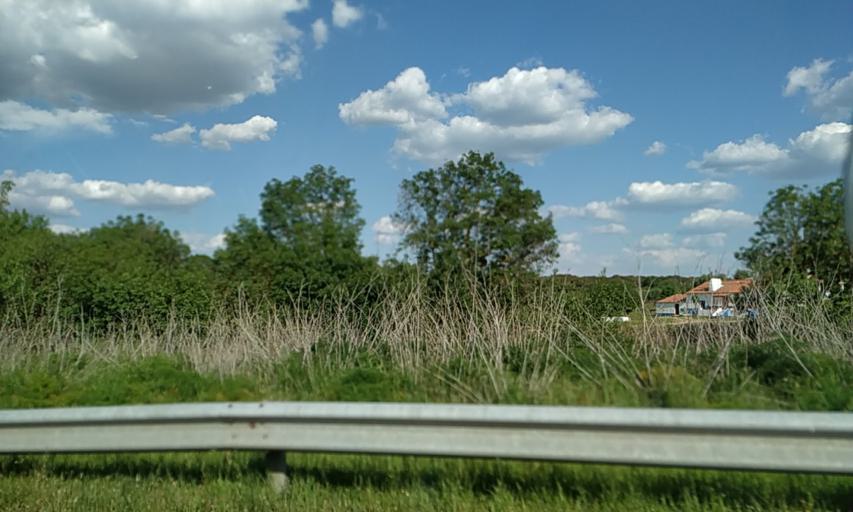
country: PT
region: Evora
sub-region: Estremoz
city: Estremoz
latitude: 38.8775
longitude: -7.5621
